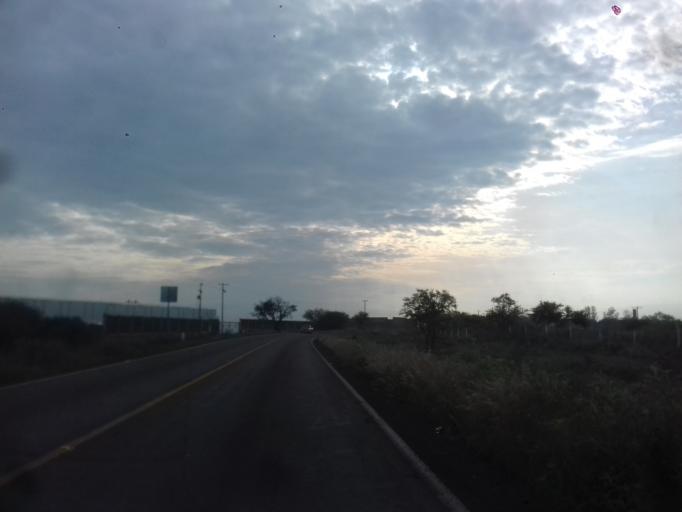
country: MX
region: Aguascalientes
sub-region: Aguascalientes
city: San Sebastian [Fraccionamiento]
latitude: 21.7997
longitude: -102.2520
